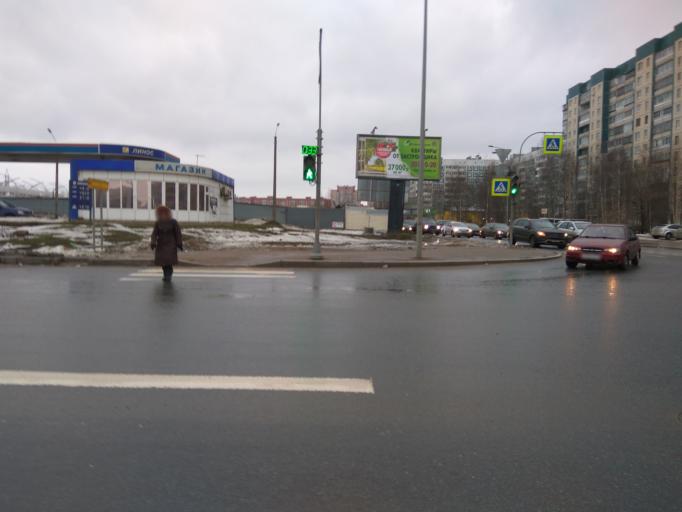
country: RU
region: St.-Petersburg
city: Staraya Derevnya
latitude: 60.0040
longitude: 30.2348
